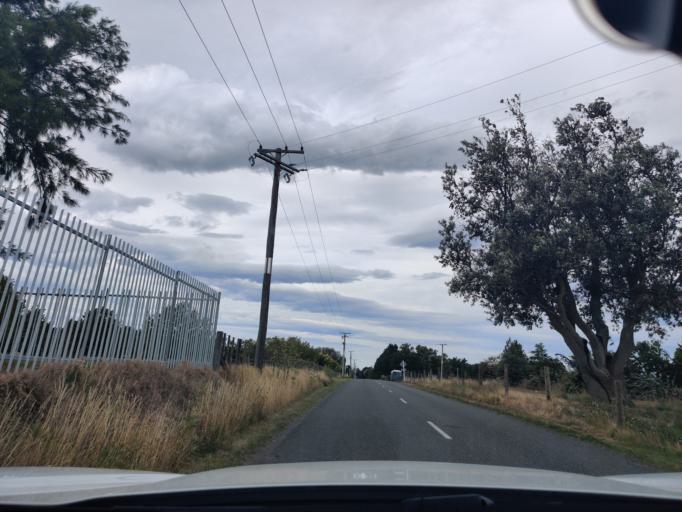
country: NZ
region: Wellington
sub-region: Masterton District
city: Masterton
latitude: -41.0395
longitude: 175.5005
